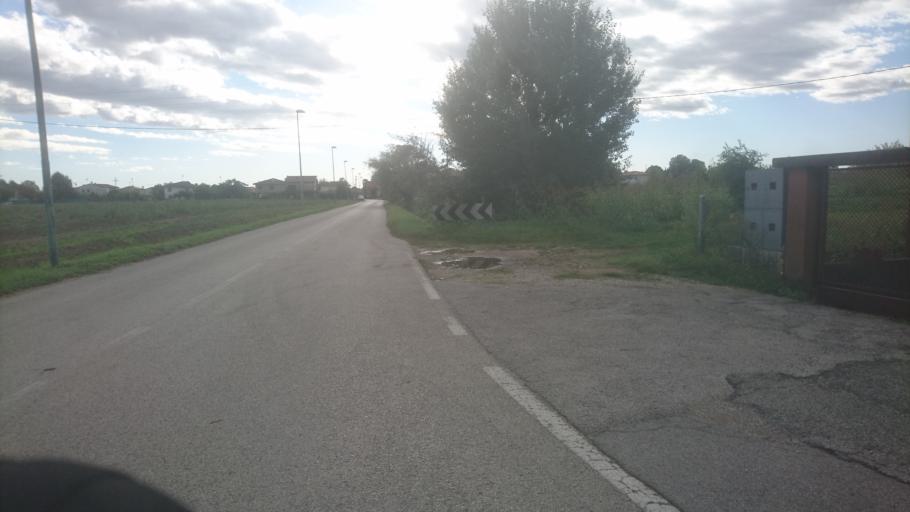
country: IT
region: Veneto
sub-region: Provincia di Padova
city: Abano Terme
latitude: 45.3522
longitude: 11.8099
